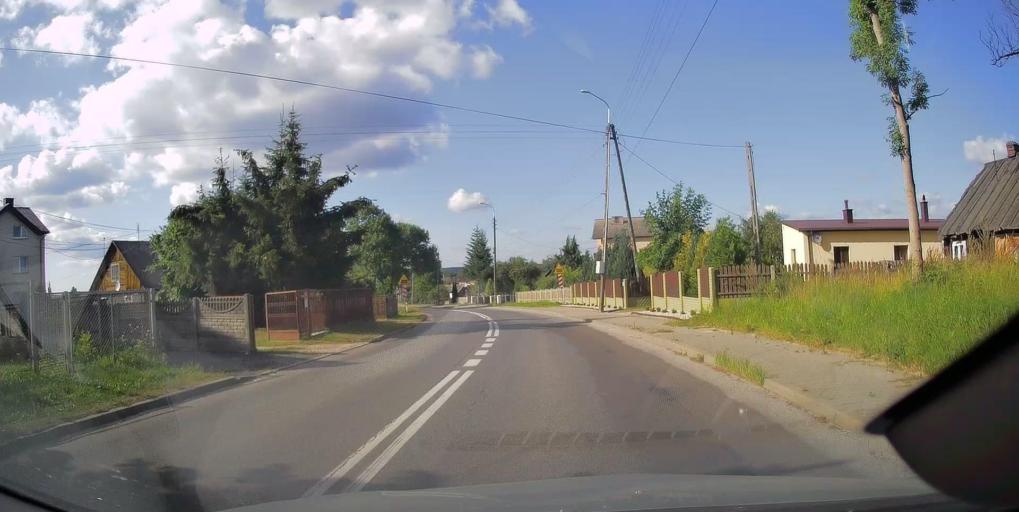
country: PL
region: Swietokrzyskie
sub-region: Powiat skarzyski
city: Suchedniow
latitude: 51.0225
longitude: 20.8379
